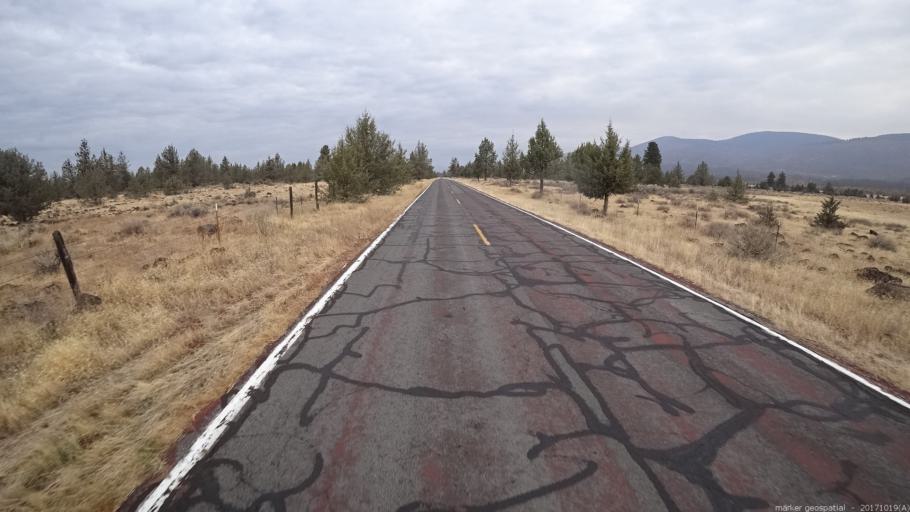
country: US
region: California
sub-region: Shasta County
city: Burney
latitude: 41.0996
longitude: -121.3225
